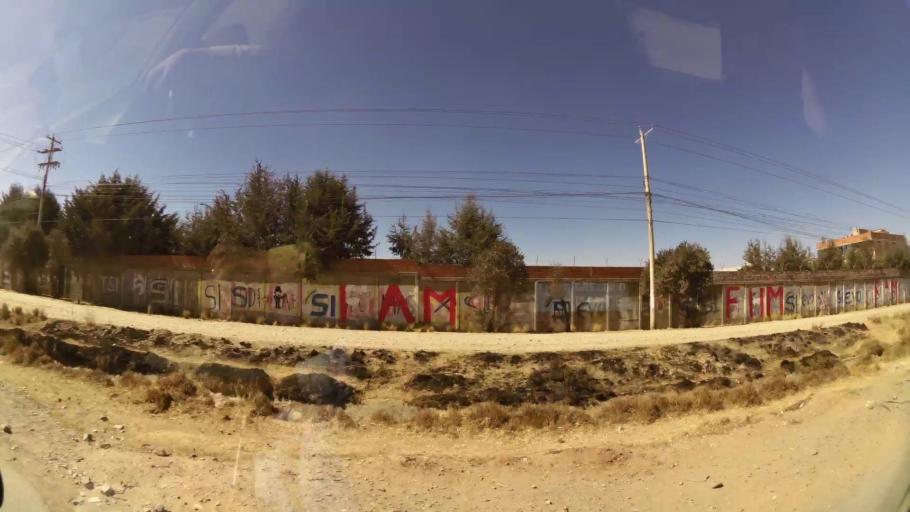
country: BO
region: La Paz
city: La Paz
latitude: -16.5487
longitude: -68.2035
